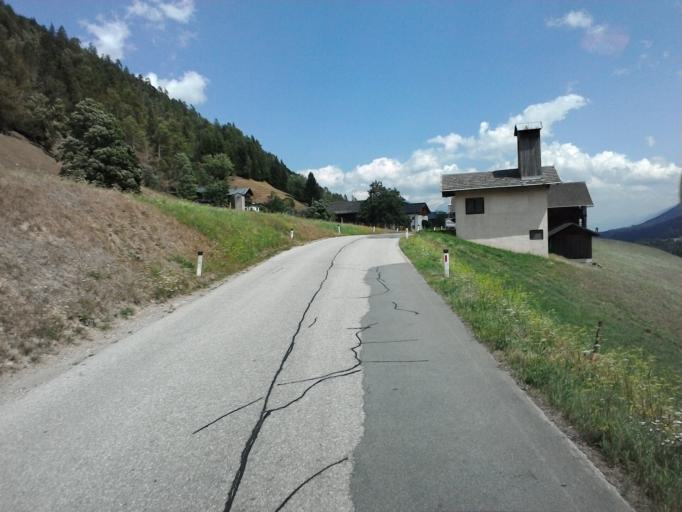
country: AT
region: Tyrol
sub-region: Politischer Bezirk Lienz
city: Nikolsdorf
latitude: 46.6860
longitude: 12.8611
